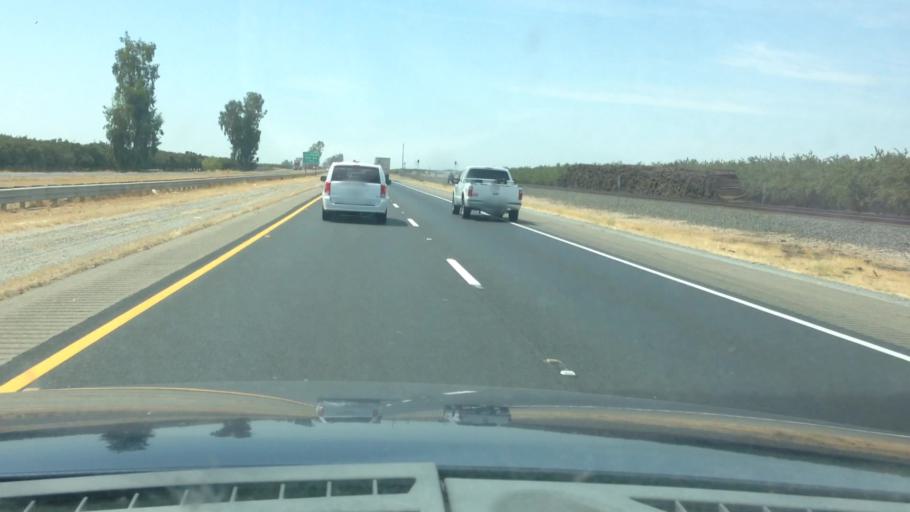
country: US
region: California
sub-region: Tulare County
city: Earlimart
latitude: 35.8595
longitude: -119.2687
